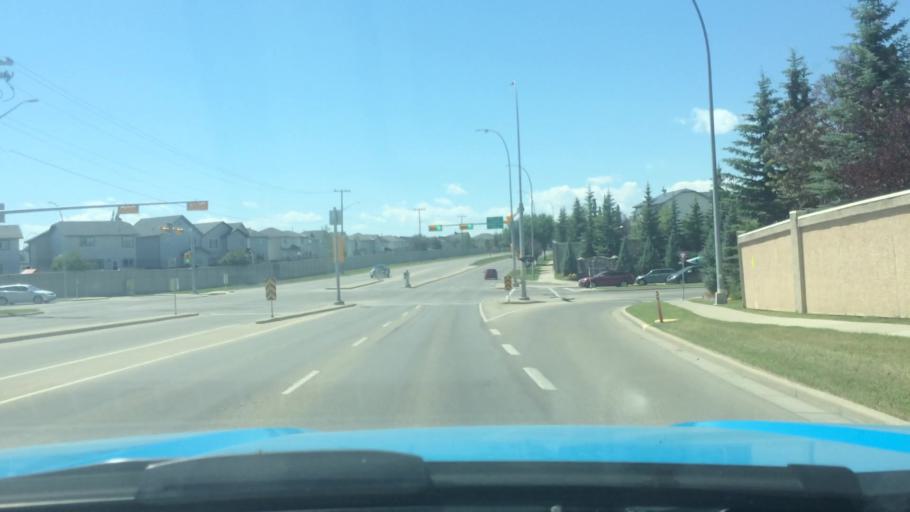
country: CA
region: Alberta
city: Calgary
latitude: 51.1490
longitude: -114.0729
